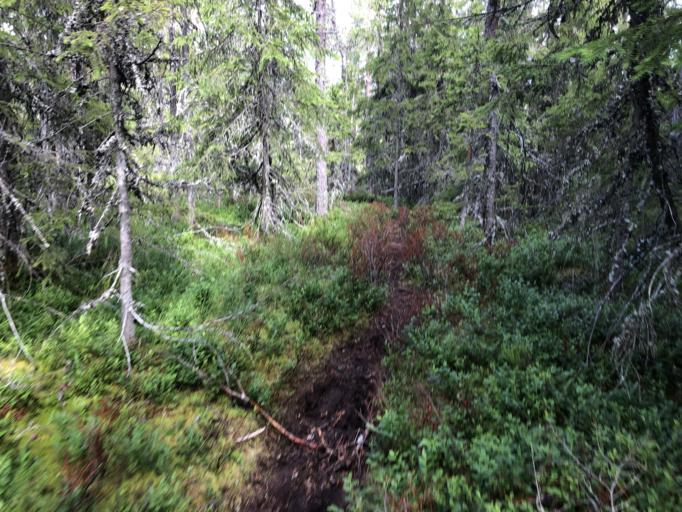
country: SE
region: Dalarna
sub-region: Vansbro Kommun
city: Jarna
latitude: 60.6655
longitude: 14.2712
